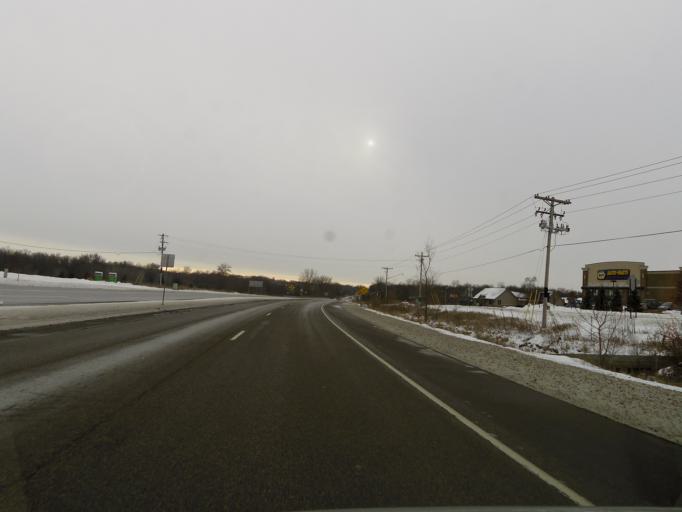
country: US
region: Minnesota
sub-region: Scott County
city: Prior Lake
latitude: 44.7416
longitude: -93.3805
